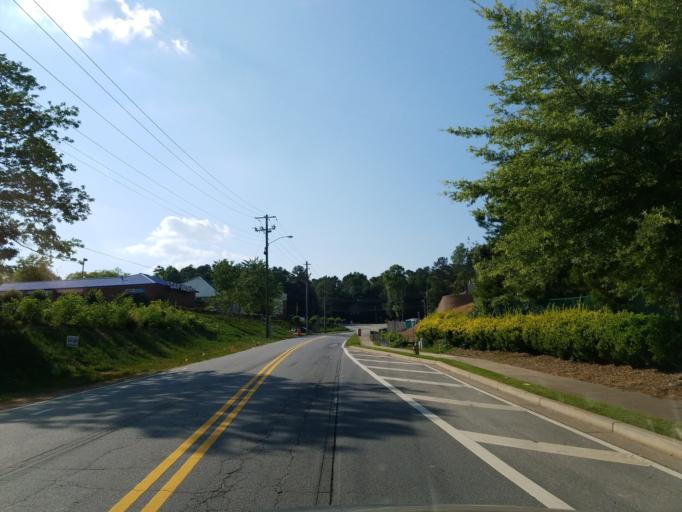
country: US
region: Georgia
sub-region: Cobb County
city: Marietta
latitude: 33.9529
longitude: -84.5786
